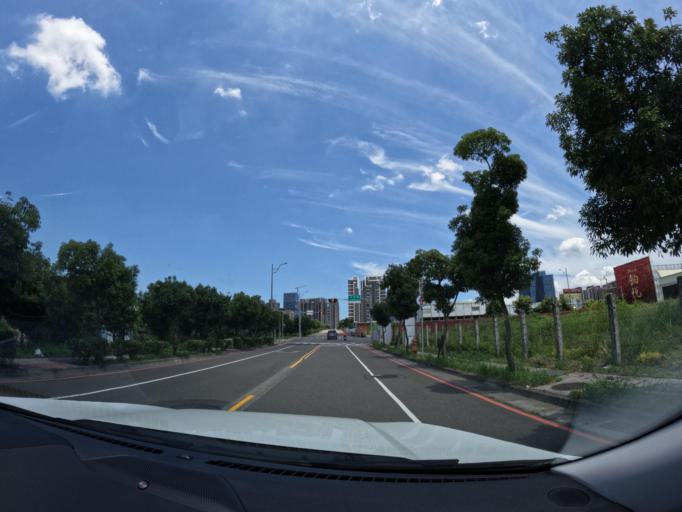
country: TW
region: Taiwan
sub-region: Taoyuan
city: Taoyuan
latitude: 25.0417
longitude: 121.3836
